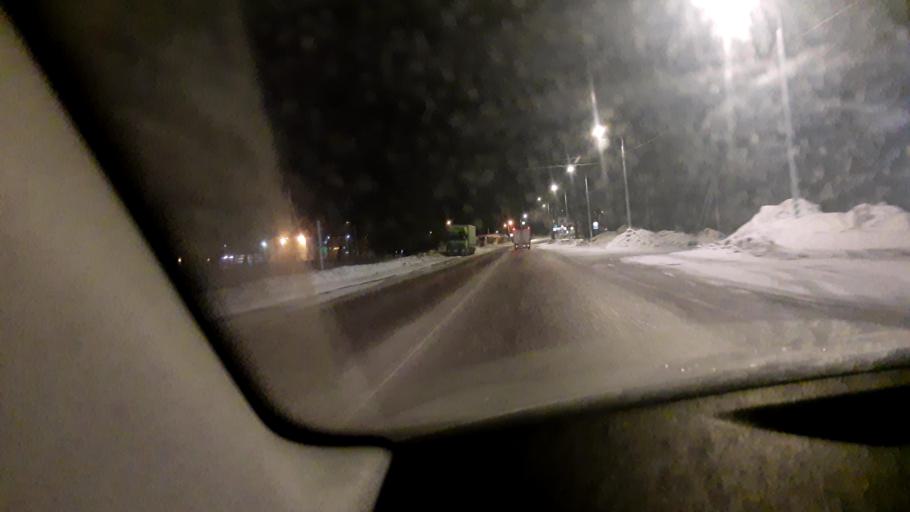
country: RU
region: Moskovskaya
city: Peresvet
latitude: 56.4476
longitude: 38.0989
